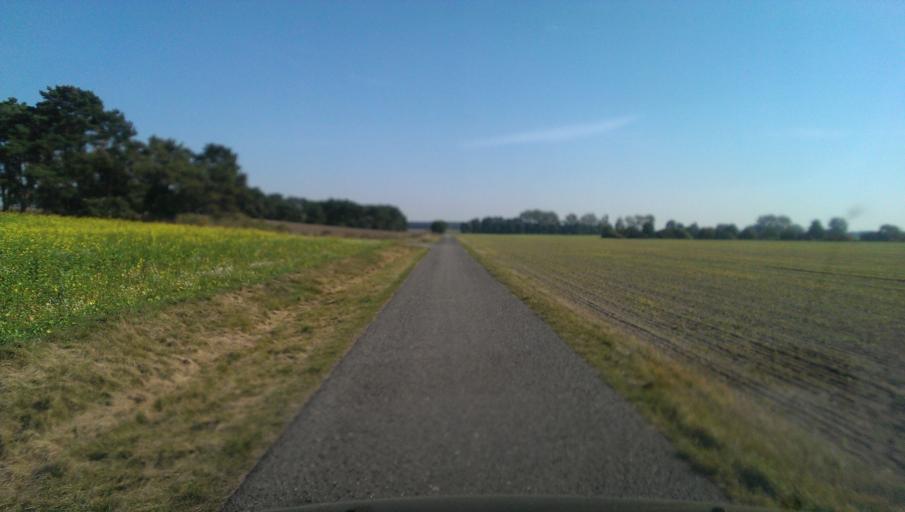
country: DE
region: Brandenburg
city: Am Mellensee
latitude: 52.2209
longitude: 13.3305
